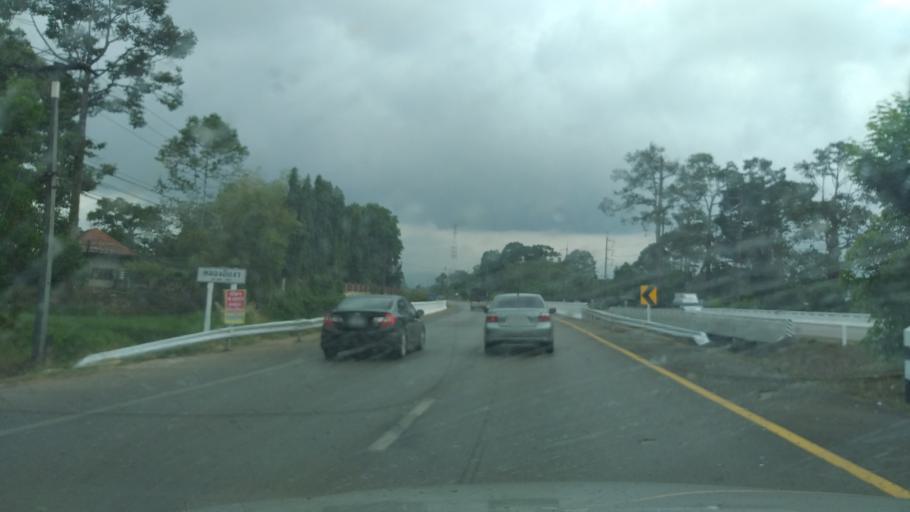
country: TH
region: Chanthaburi
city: Khlung
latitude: 12.4528
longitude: 102.2825
